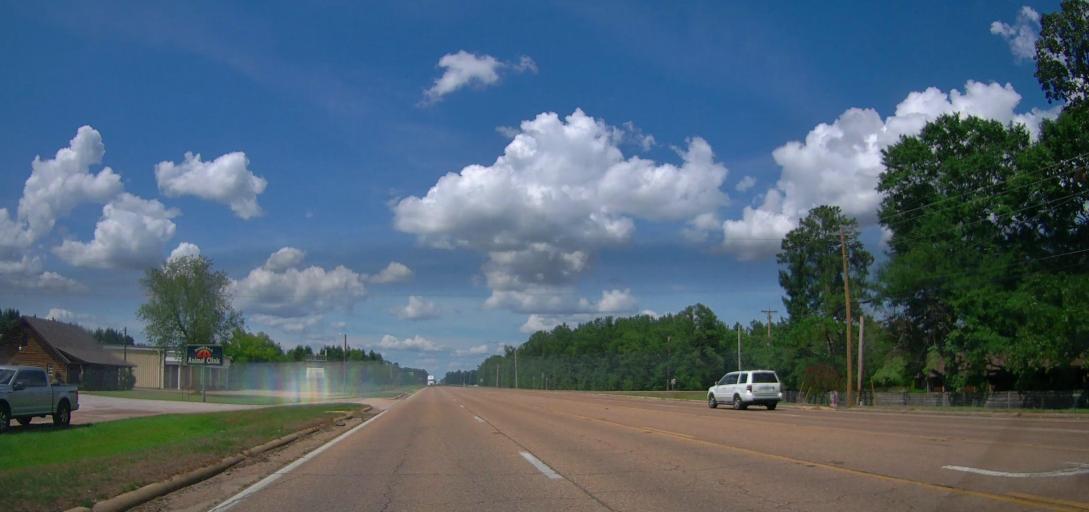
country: US
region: Mississippi
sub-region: Lowndes County
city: Columbus Air Force Base
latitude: 33.5712
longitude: -88.4313
